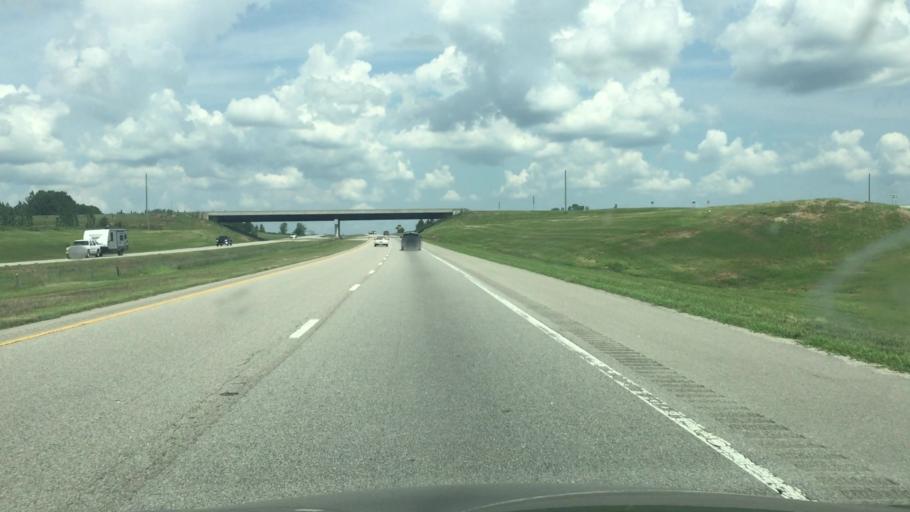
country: US
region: North Carolina
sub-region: Richmond County
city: Ellerbe
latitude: 35.1446
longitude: -79.7138
